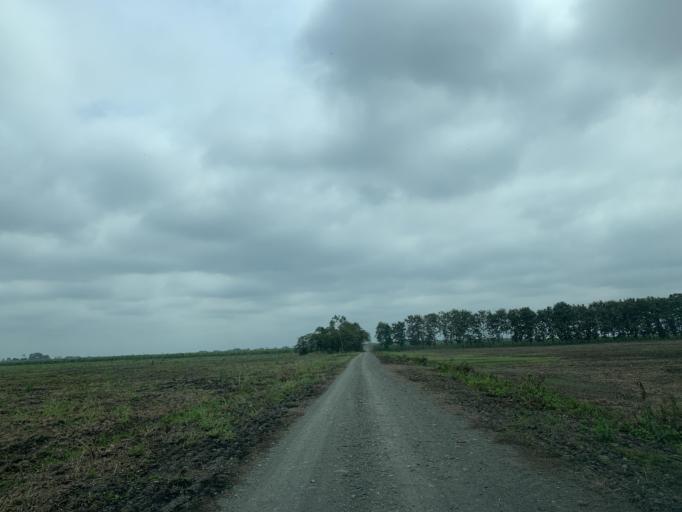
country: EC
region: Canar
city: La Troncal
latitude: -2.3567
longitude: -79.4626
